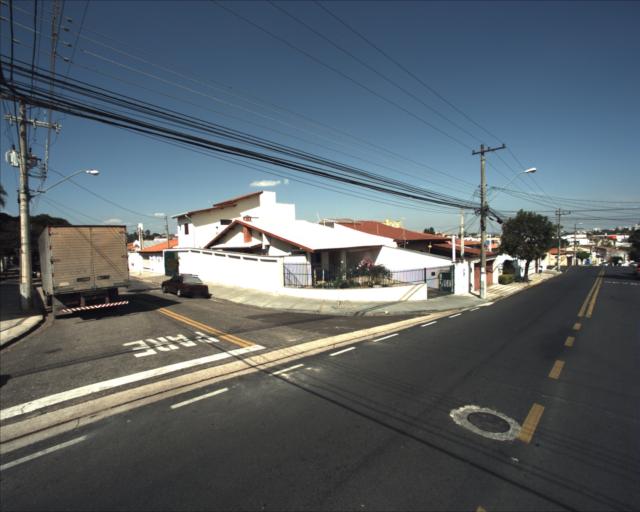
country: BR
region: Sao Paulo
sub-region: Sorocaba
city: Sorocaba
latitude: -23.4722
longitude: -47.4374
